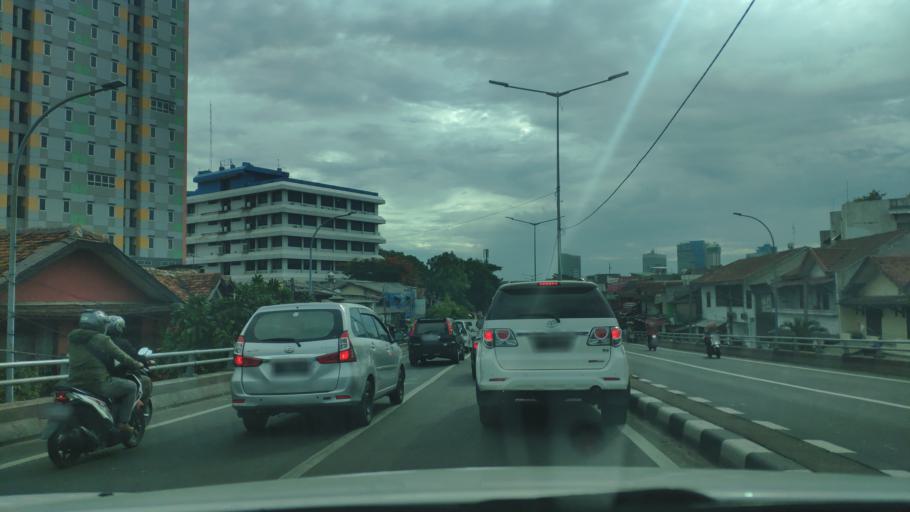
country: ID
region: Jakarta Raya
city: Jakarta
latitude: -6.1856
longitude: 106.8097
